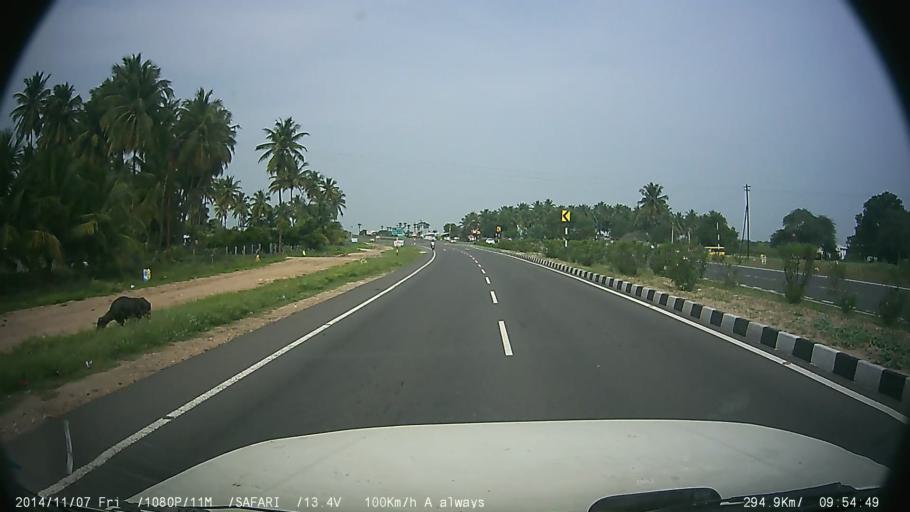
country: IN
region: Tamil Nadu
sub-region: Erode
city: Vijayapuri
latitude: 11.2389
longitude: 77.4987
